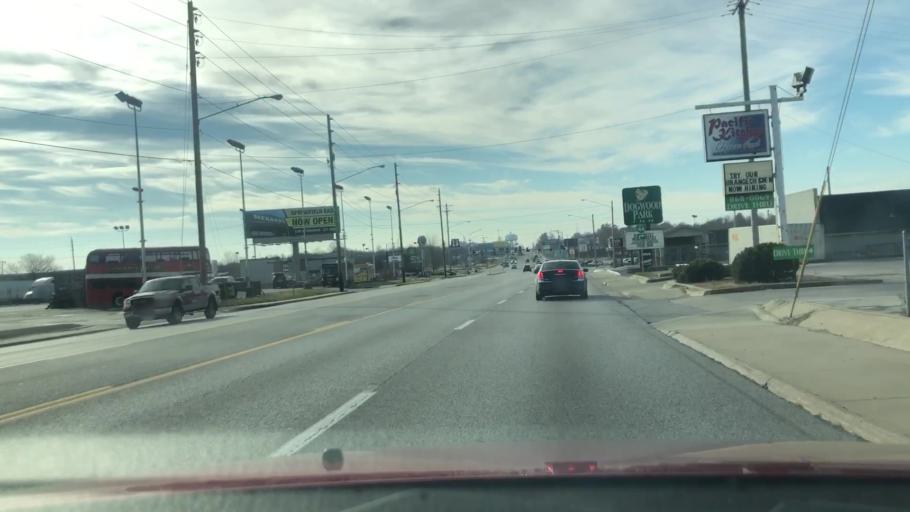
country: US
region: Missouri
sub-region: Greene County
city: Springfield
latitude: 37.2169
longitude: -93.2617
